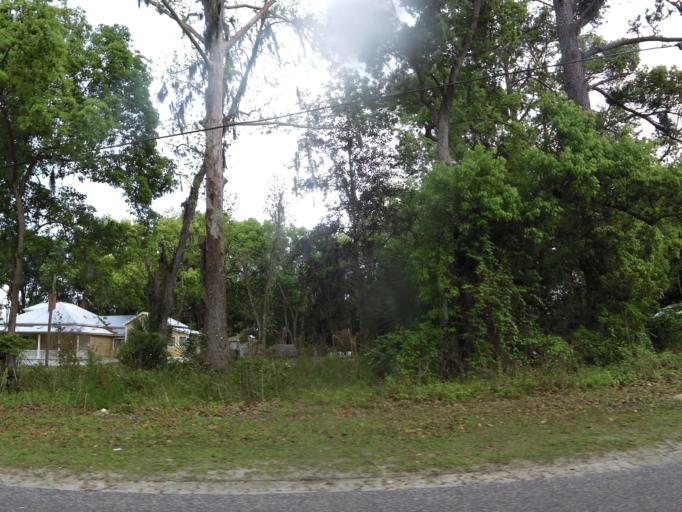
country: US
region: Florida
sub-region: Nassau County
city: Hilliard
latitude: 30.6895
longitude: -81.9204
